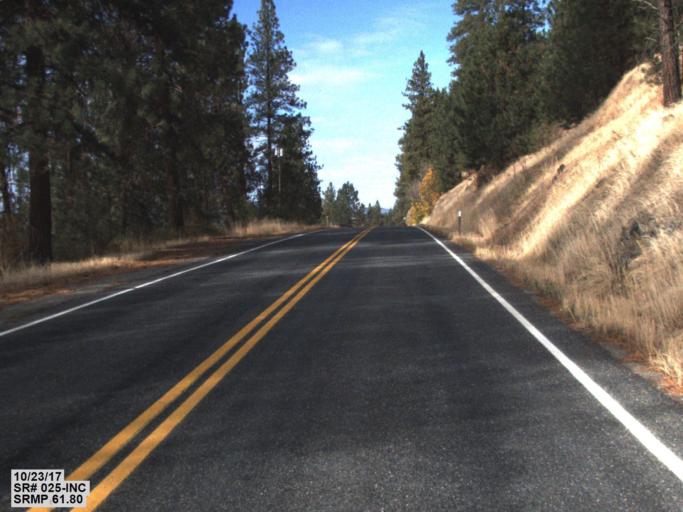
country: US
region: Washington
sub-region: Stevens County
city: Kettle Falls
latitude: 48.3639
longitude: -118.1634
